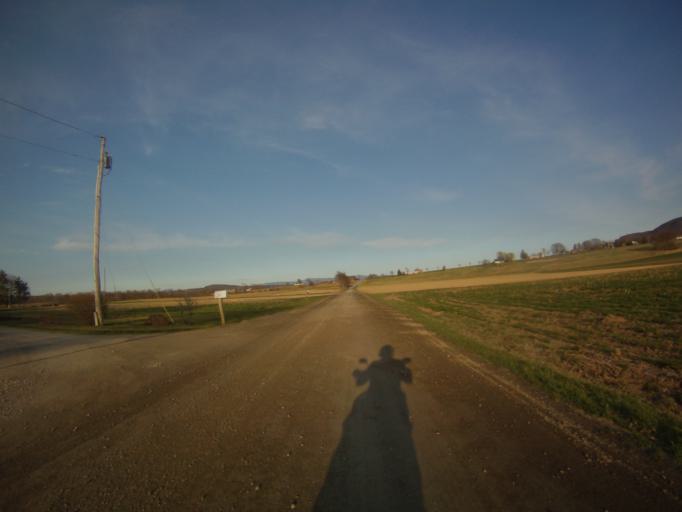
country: US
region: Vermont
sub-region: Addison County
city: Vergennes
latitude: 44.0960
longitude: -73.3083
